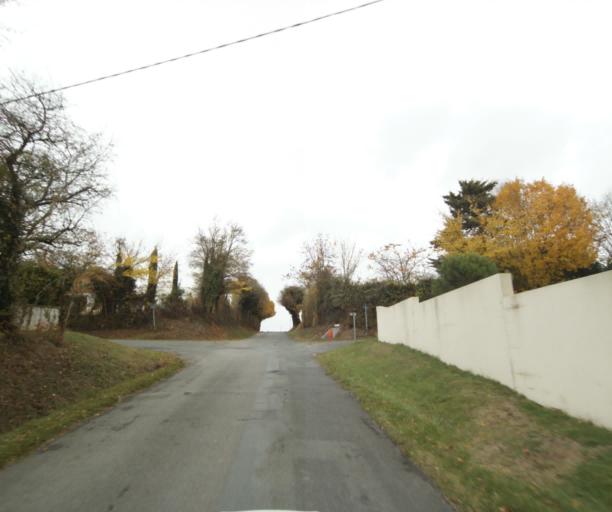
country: FR
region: Poitou-Charentes
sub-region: Departement de la Charente-Maritime
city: Bussac-sur-Charente
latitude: 45.7706
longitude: -0.6436
